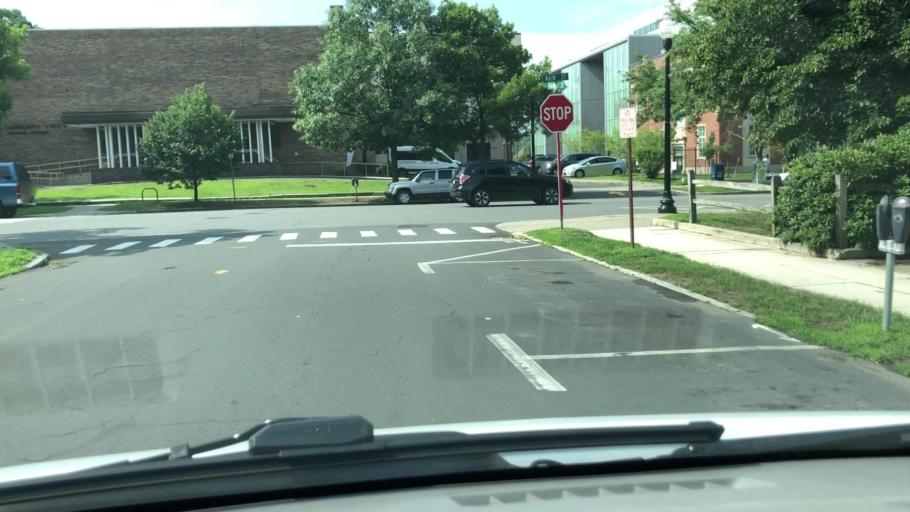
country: US
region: Massachusetts
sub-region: Franklin County
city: Greenfield
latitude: 42.5878
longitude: -72.5974
